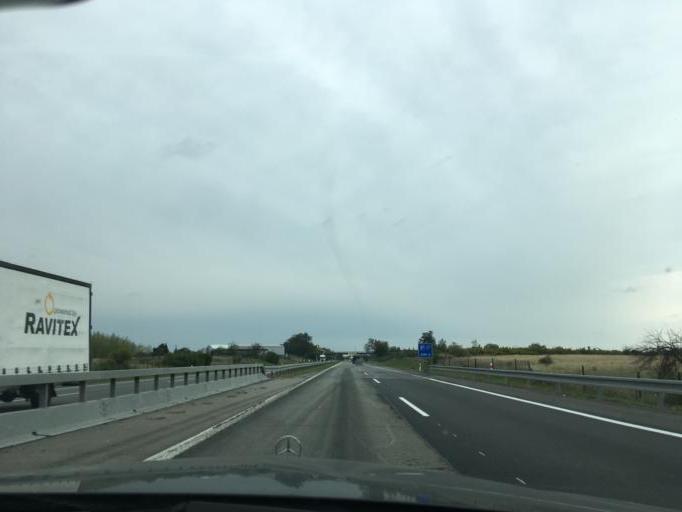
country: CZ
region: South Moravian
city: Kostice
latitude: 48.7476
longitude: 16.9635
